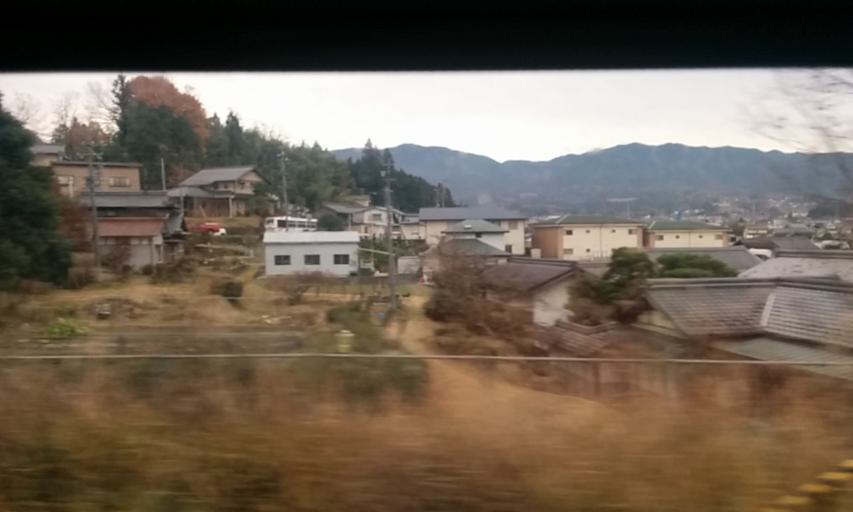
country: JP
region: Gifu
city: Nakatsugawa
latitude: 35.4778
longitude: 137.4448
